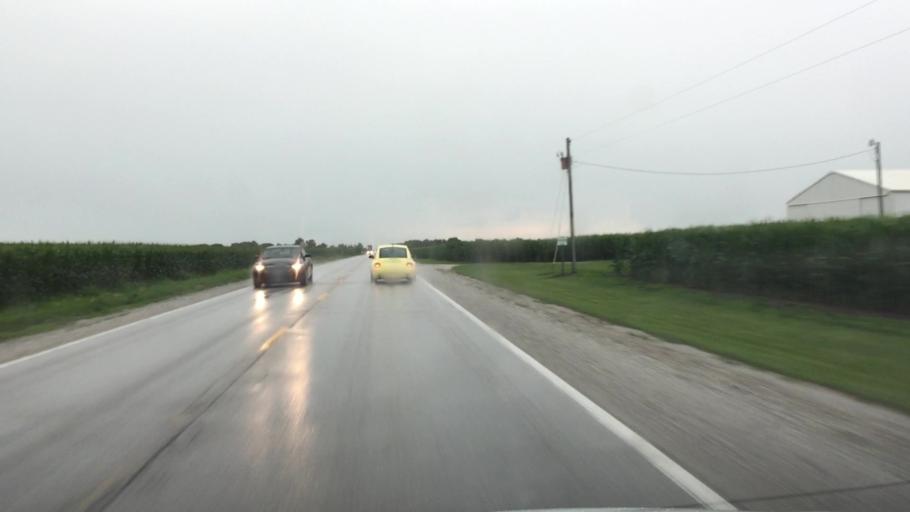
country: US
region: Illinois
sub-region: Hancock County
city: Carthage
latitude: 40.4483
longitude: -91.1398
